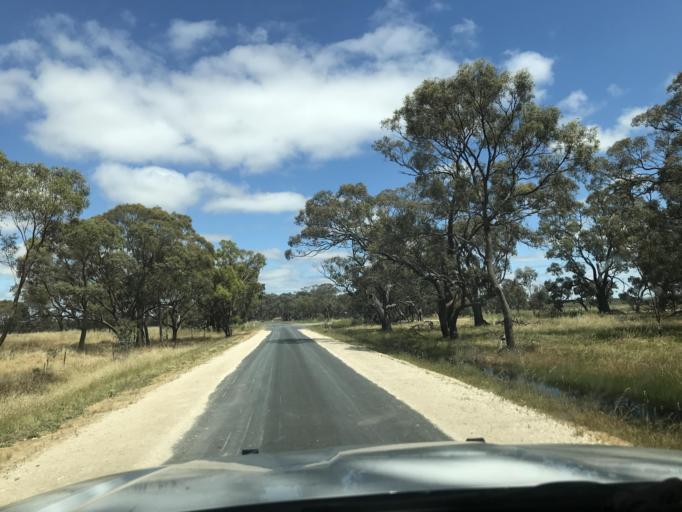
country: AU
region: South Australia
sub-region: Tatiara
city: Bordertown
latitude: -36.3085
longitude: 141.0428
